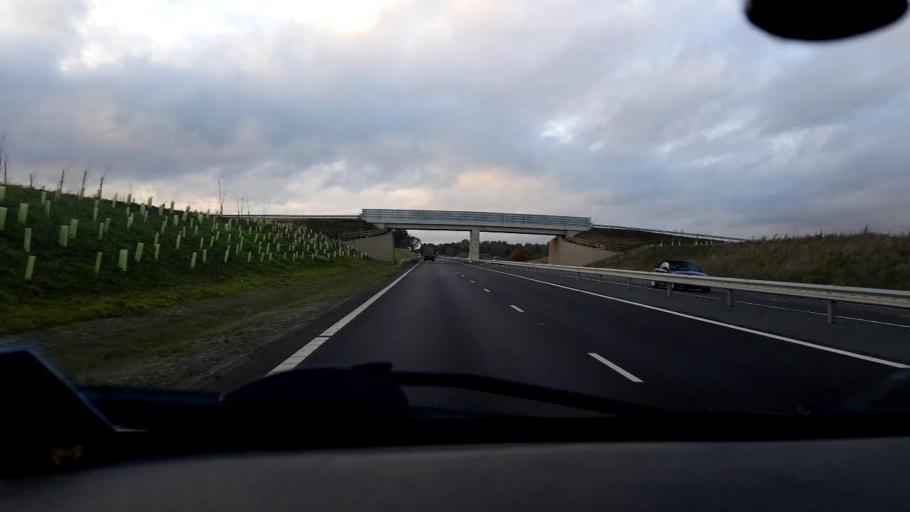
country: GB
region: England
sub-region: Norfolk
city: Horsford
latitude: 52.6925
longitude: 1.2261
